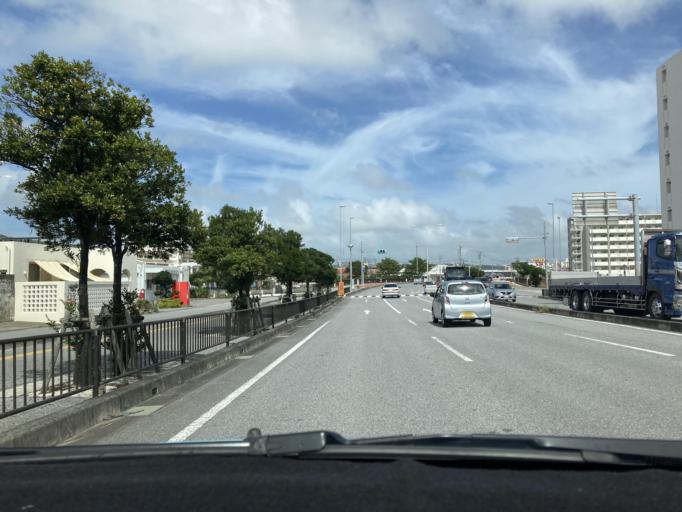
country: JP
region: Okinawa
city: Ginowan
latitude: 26.2015
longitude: 127.7604
